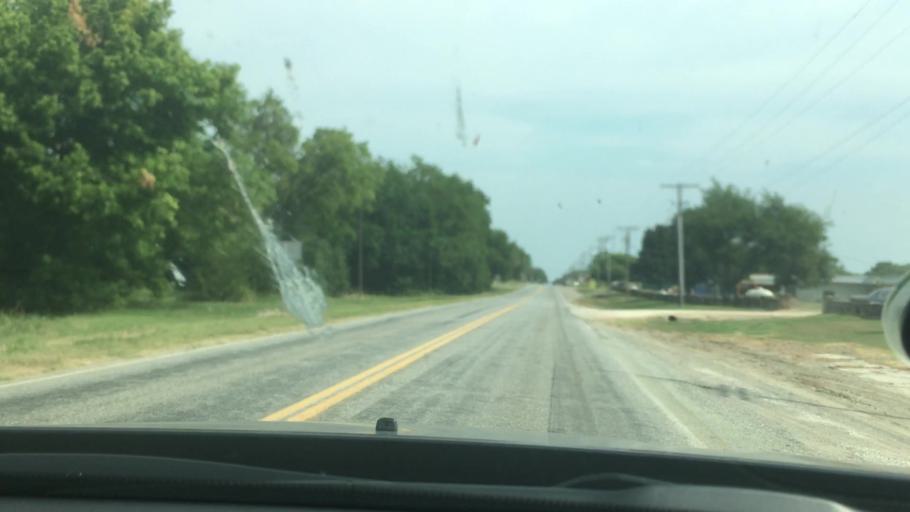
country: US
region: Oklahoma
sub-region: Coal County
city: Coalgate
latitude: 34.3693
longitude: -96.4245
